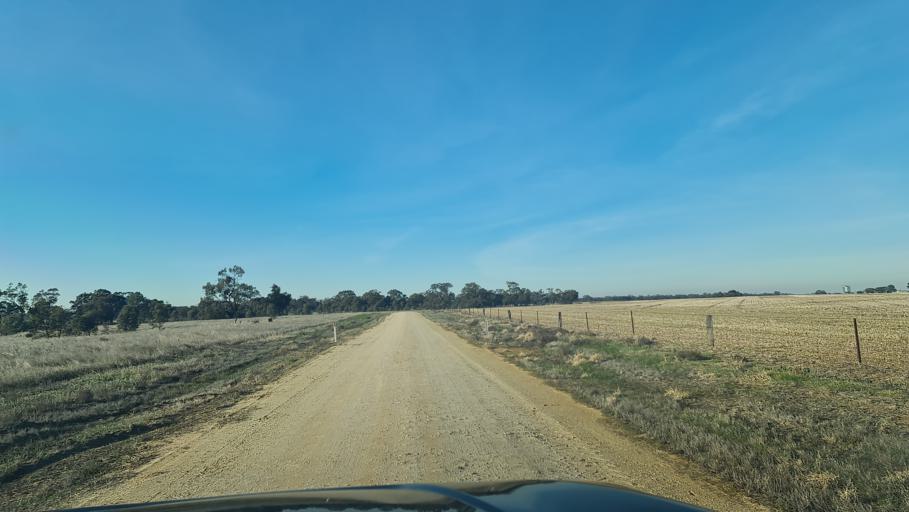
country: AU
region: Victoria
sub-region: Horsham
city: Horsham
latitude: -36.3547
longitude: 142.3948
